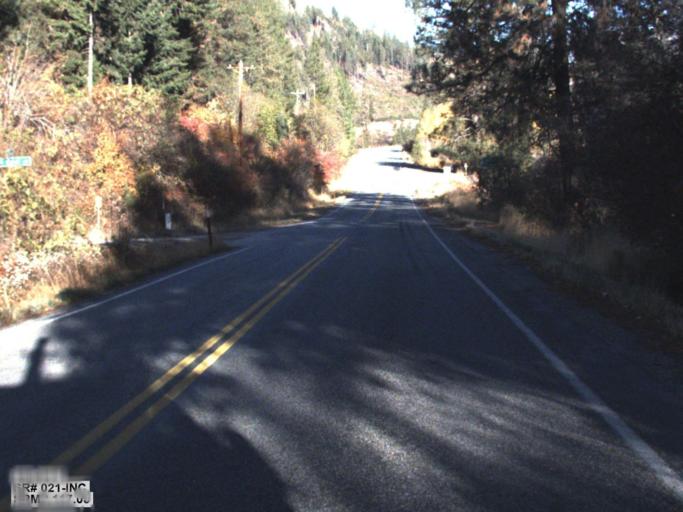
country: US
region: Washington
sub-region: Okanogan County
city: Coulee Dam
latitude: 48.0817
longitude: -118.6895
